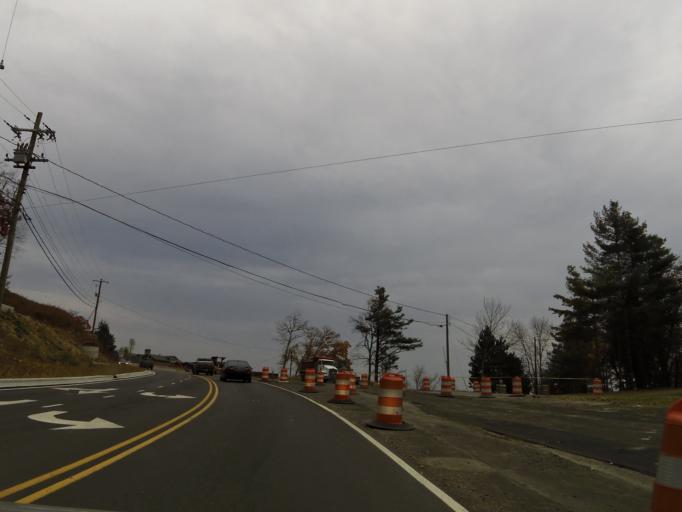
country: US
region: North Carolina
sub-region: Watauga County
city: Blowing Rock
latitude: 36.1216
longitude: -81.6711
